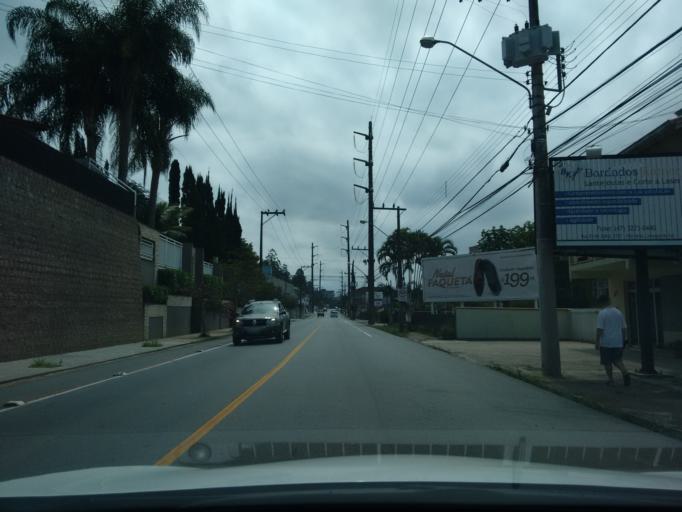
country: BR
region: Santa Catarina
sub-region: Jaragua Do Sul
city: Jaragua do Sul
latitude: -26.4957
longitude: -49.0741
